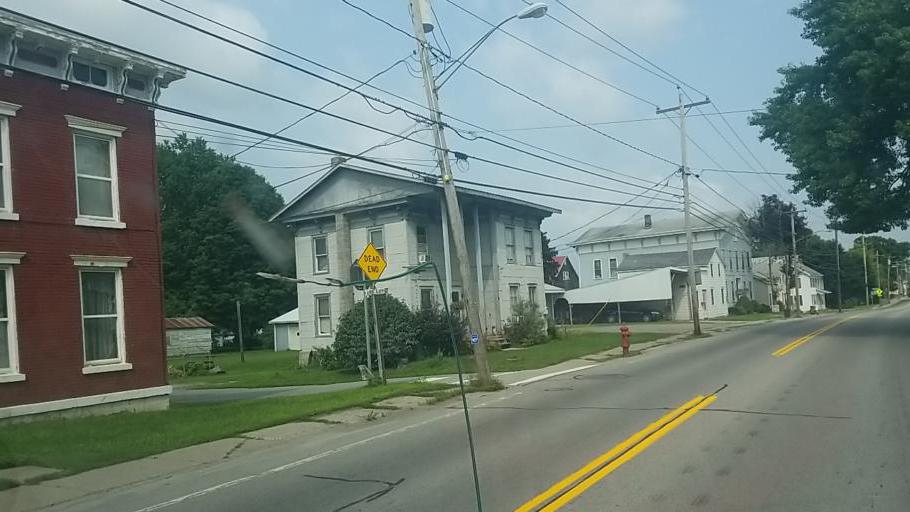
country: US
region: New York
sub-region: Montgomery County
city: Fort Plain
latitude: 42.9317
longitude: -74.6117
